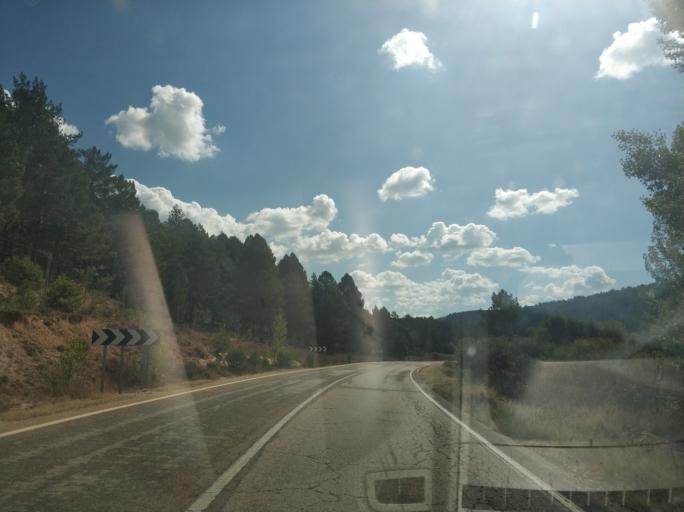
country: ES
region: Castille and Leon
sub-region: Provincia de Soria
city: San Leonardo de Yague
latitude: 41.8205
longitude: -3.0693
